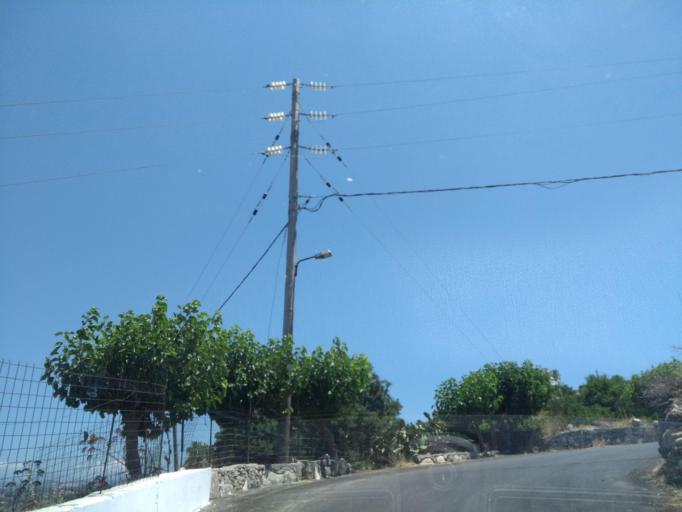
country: GR
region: Crete
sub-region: Nomos Chanias
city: Georgioupolis
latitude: 35.3138
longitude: 24.3099
